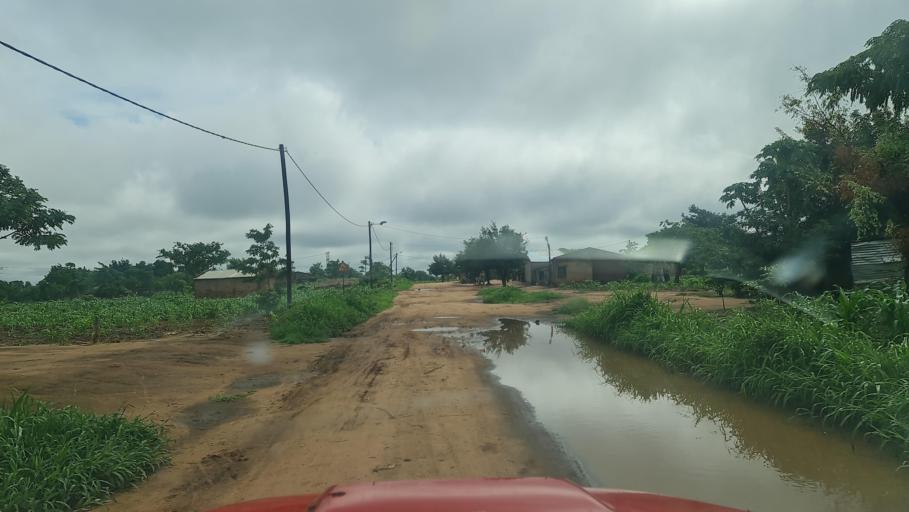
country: MW
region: Southern Region
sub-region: Nsanje District
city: Nsanje
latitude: -17.2212
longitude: 35.6708
